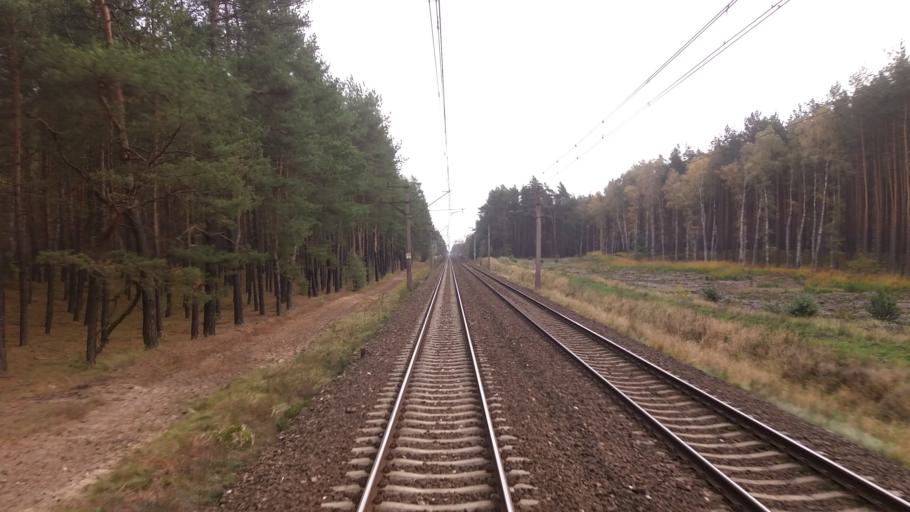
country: PL
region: West Pomeranian Voivodeship
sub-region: Powiat stargardzki
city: Kobylanka
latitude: 53.3804
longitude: 14.7898
